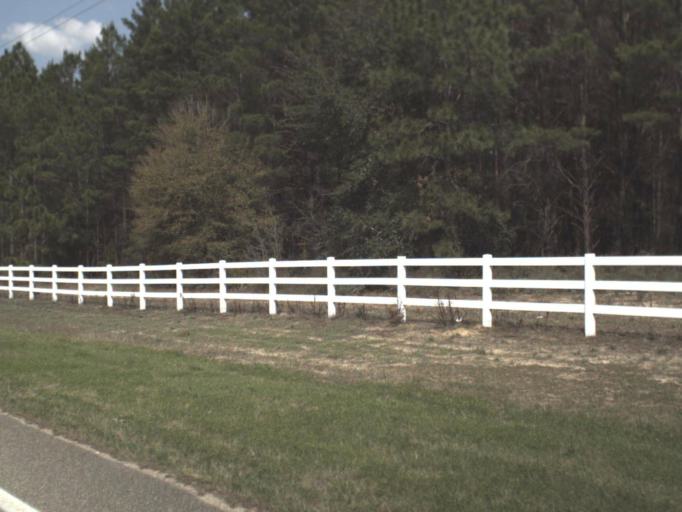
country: US
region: Florida
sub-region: Liberty County
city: Bristol
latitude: 30.4211
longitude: -84.9021
